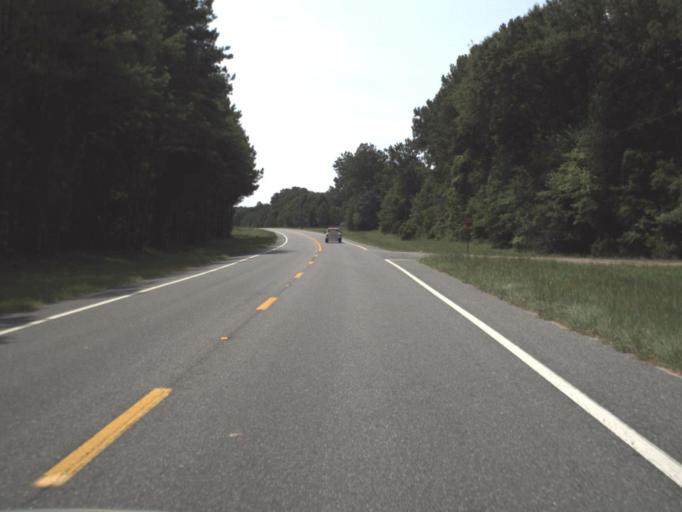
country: US
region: Georgia
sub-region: Echols County
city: Statenville
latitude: 30.5856
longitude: -83.0914
